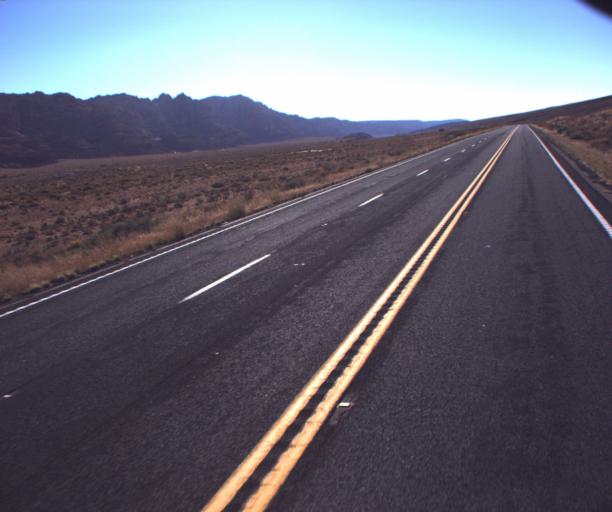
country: US
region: Arizona
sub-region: Coconino County
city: LeChee
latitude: 36.5659
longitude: -111.6384
